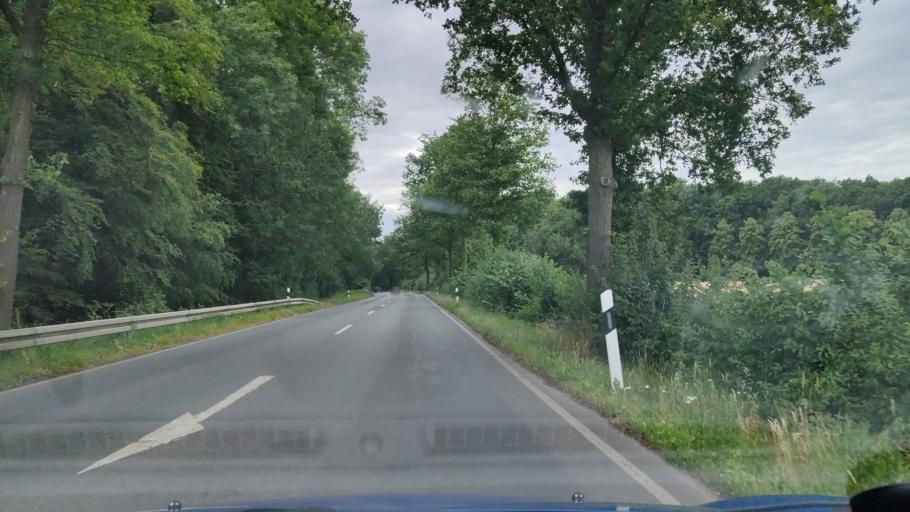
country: DE
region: Lower Saxony
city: Ronnenberg
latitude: 52.3109
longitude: 9.6777
